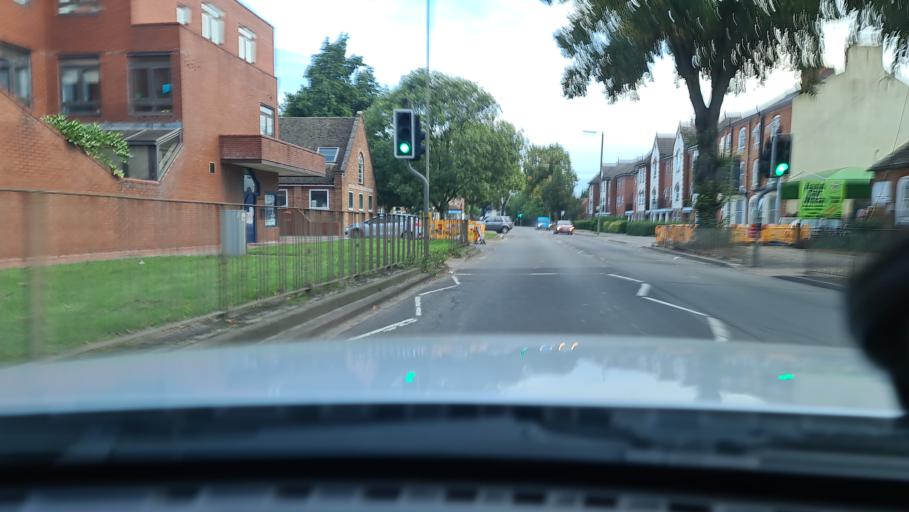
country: GB
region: England
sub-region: Oxfordshire
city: Banbury
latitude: 52.0644
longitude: -1.3397
